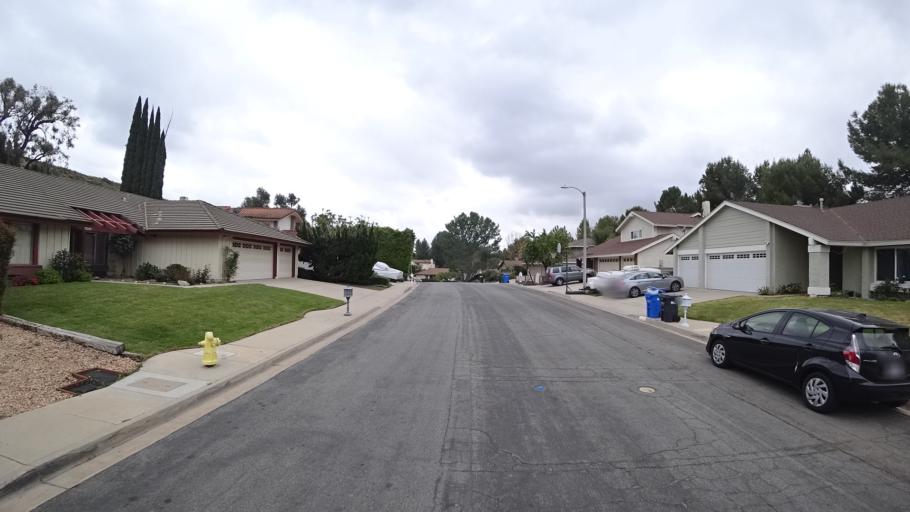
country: US
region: California
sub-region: Ventura County
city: Moorpark
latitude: 34.2216
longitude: -118.8881
